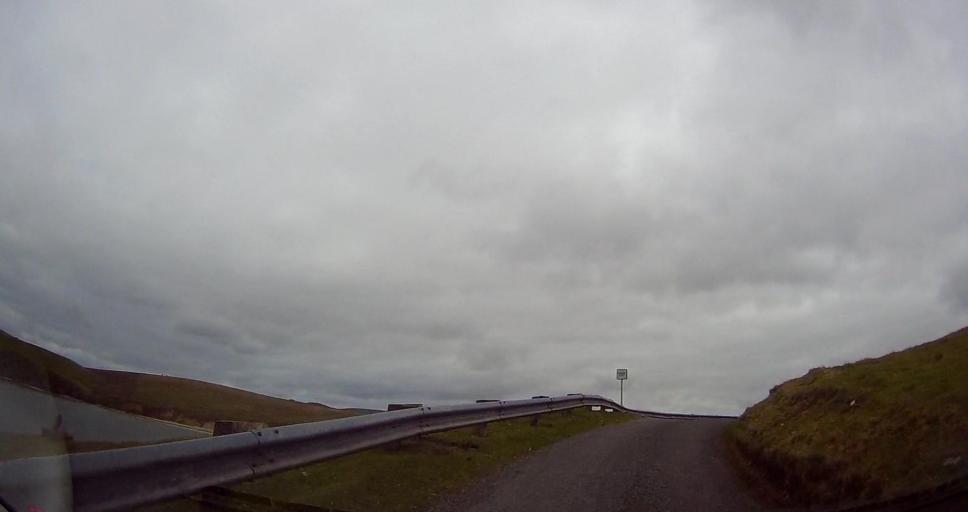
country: GB
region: Scotland
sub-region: Shetland Islands
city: Shetland
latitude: 60.8092
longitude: -0.8788
